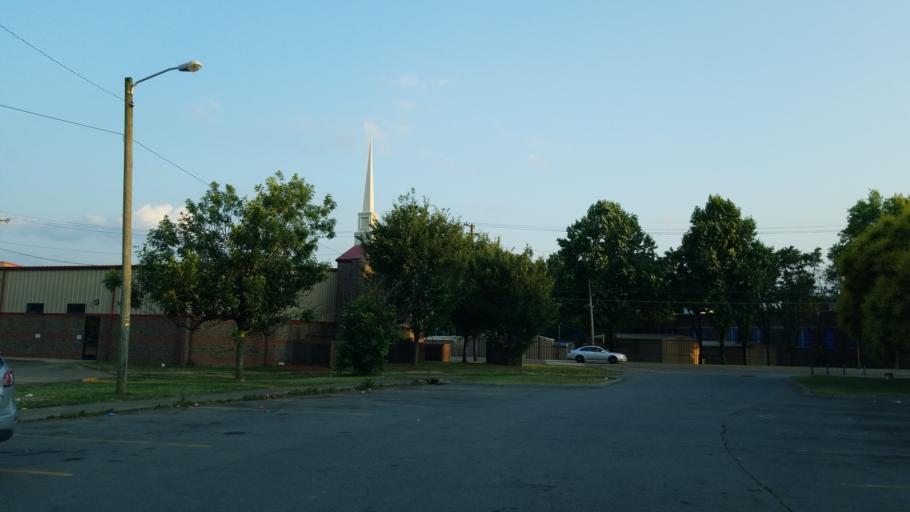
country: US
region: Tennessee
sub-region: Davidson County
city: Nashville
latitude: 36.1498
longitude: -86.7634
